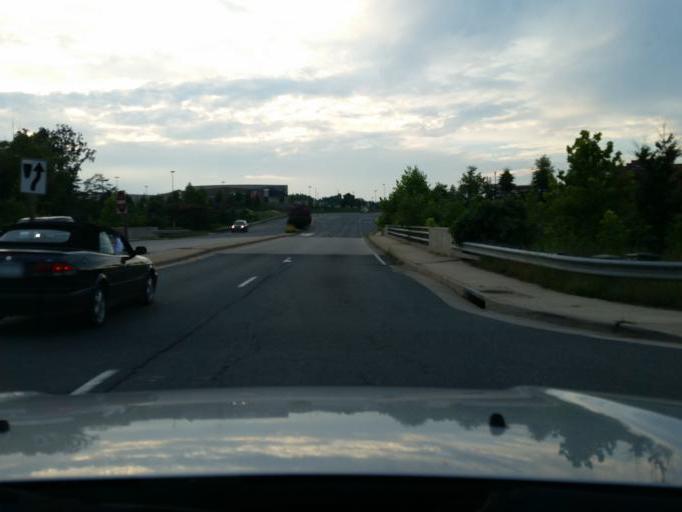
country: US
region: Virginia
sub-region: City of Fredericksburg
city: Fredericksburg
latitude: 38.2339
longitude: -77.5049
